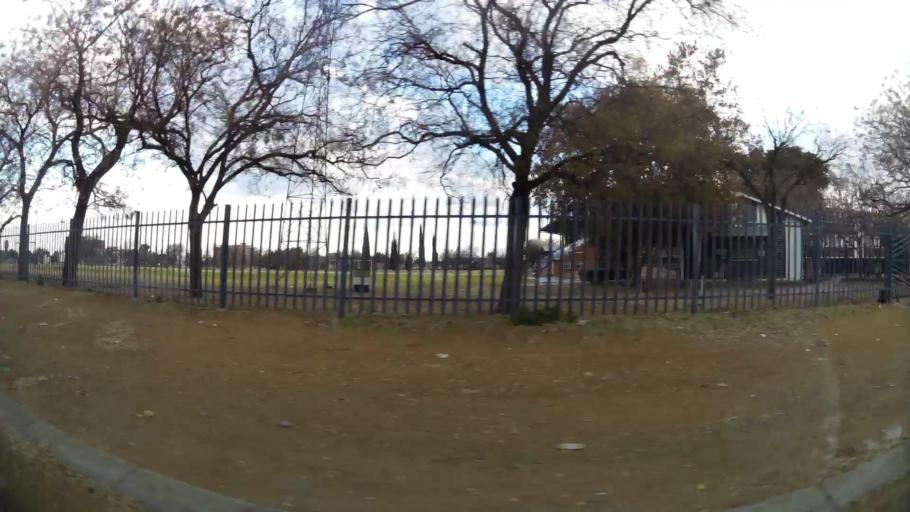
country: ZA
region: Orange Free State
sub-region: Lejweleputswa District Municipality
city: Welkom
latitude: -27.9792
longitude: 26.7277
